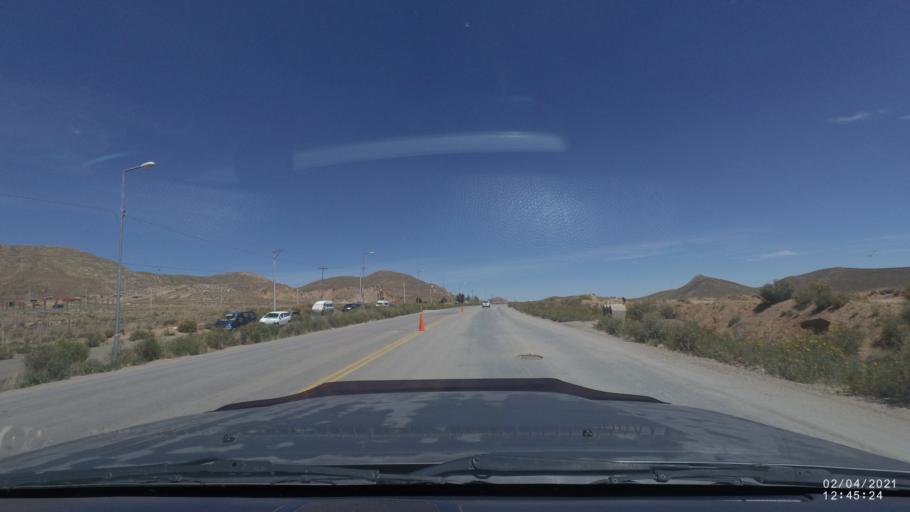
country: BO
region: Oruro
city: Oruro
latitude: -17.9352
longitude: -67.1335
